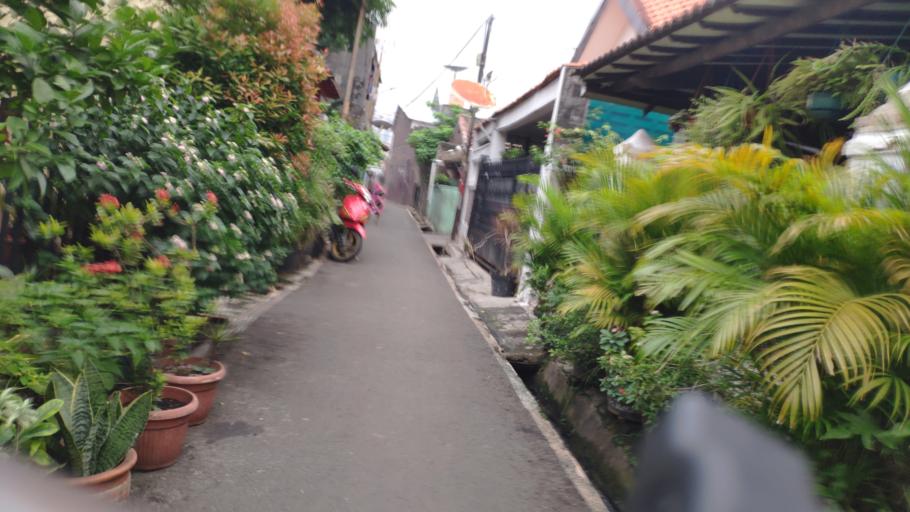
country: ID
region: Jakarta Raya
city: Jakarta
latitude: -6.2135
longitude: 106.8402
